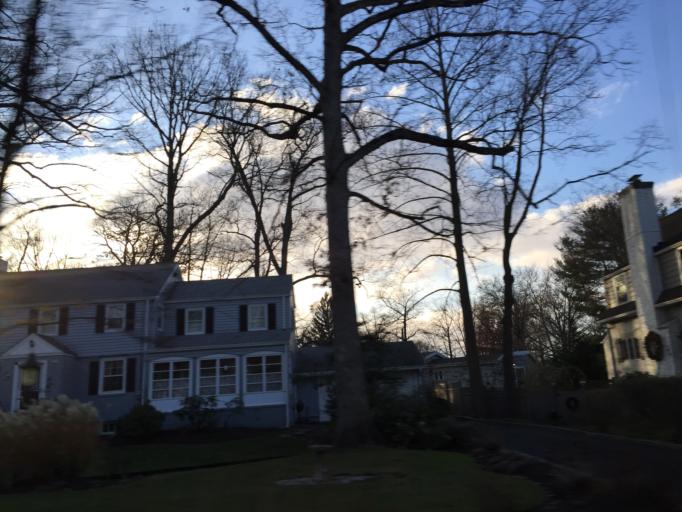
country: US
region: New Jersey
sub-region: Union County
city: Summit
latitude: 40.7264
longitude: -74.3678
